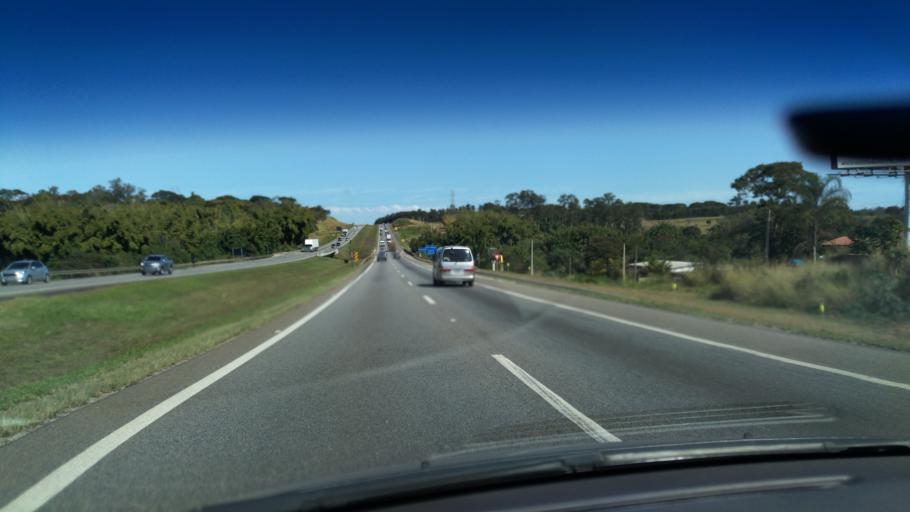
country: BR
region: Sao Paulo
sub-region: Jaguariuna
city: Jaguariuna
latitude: -22.7354
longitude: -47.0170
